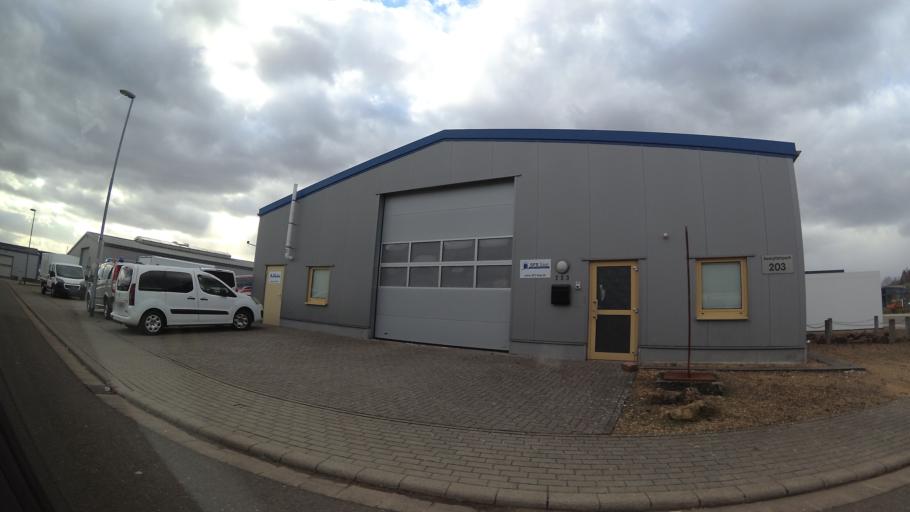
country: DE
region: Saarland
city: Bexbach
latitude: 49.3592
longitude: 7.2747
